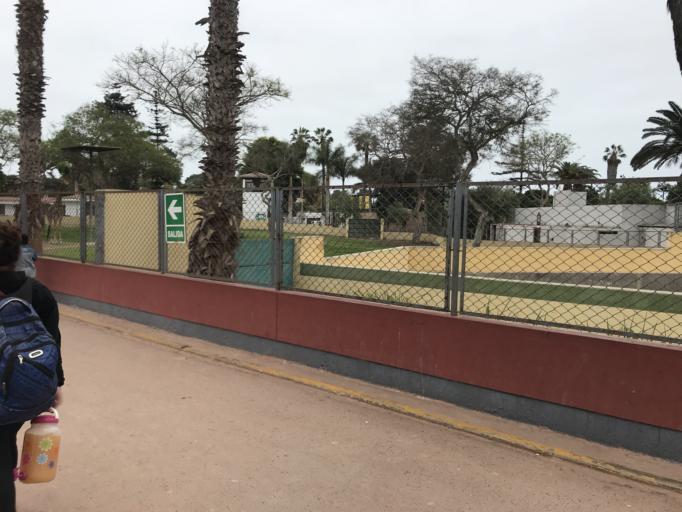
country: PE
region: Callao
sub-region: Callao
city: Callao
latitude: -12.0683
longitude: -77.0847
